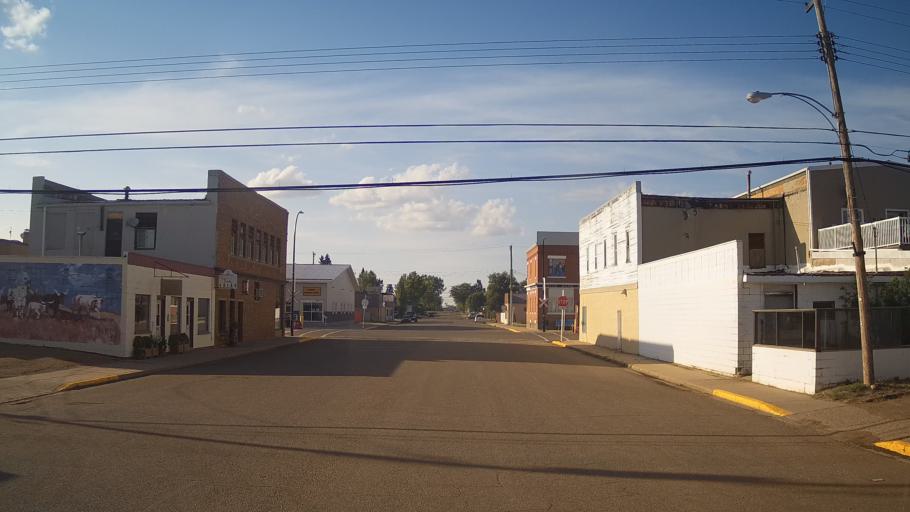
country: CA
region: Alberta
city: Hanna
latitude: 51.6420
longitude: -111.9285
